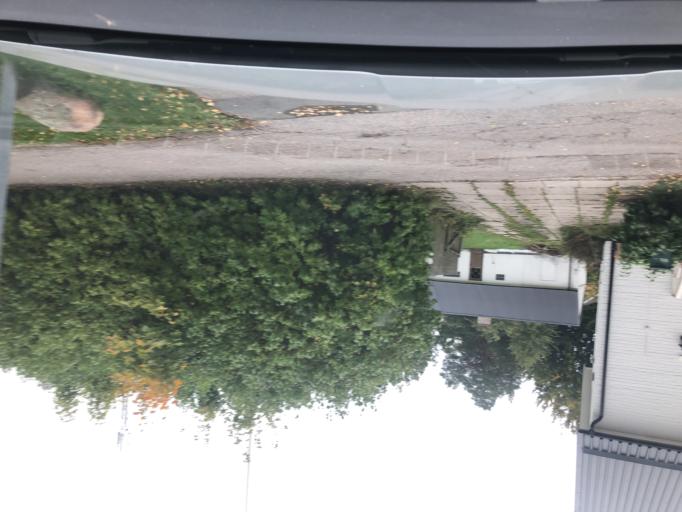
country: SE
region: Uppsala
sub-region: Osthammars Kommun
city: Gimo
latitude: 60.1735
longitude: 18.1876
